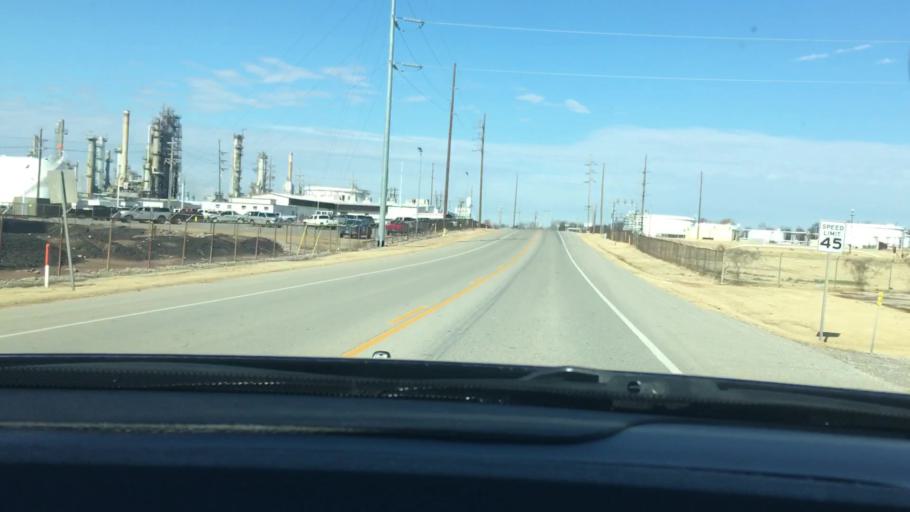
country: US
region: Oklahoma
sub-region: Garvin County
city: Wynnewood
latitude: 34.6297
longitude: -97.1651
